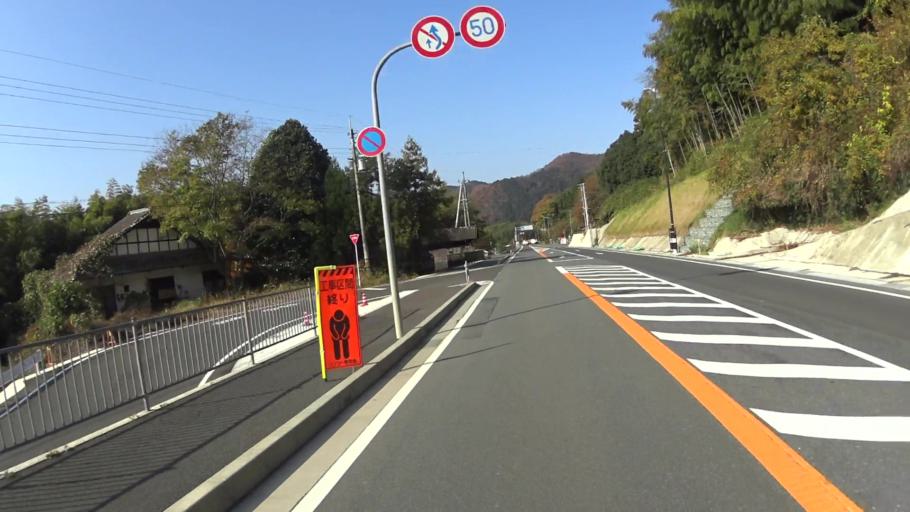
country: JP
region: Kyoto
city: Ayabe
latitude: 35.2006
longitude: 135.2521
